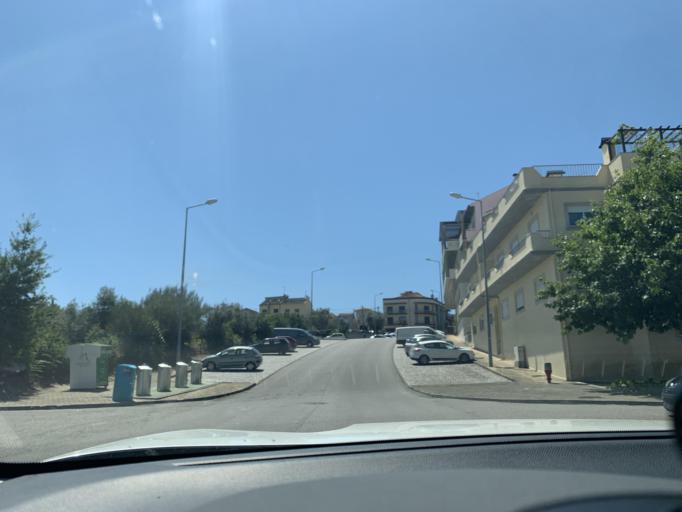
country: PT
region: Viseu
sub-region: Mangualde
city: Mangualde
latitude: 40.6065
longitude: -7.7576
